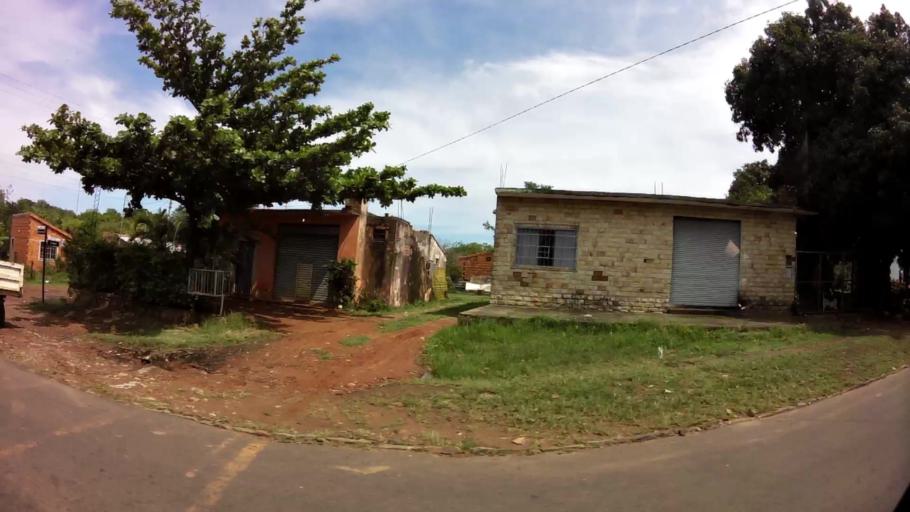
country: PY
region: Central
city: Limpio
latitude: -25.1739
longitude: -57.4423
